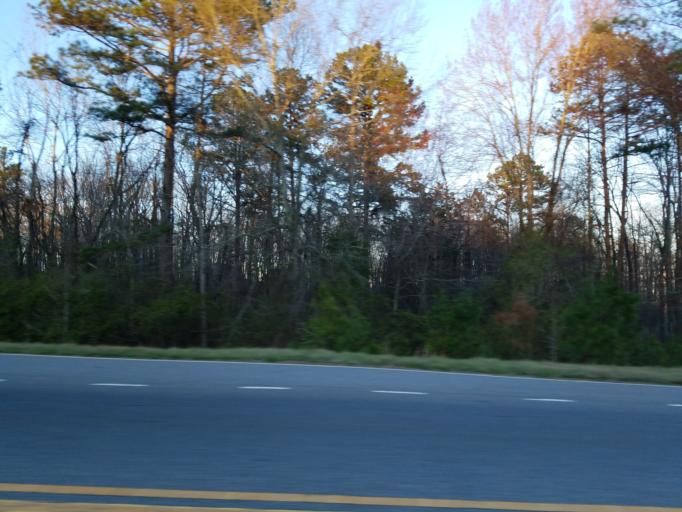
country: US
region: Georgia
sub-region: Hall County
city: Oakwood
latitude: 34.3192
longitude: -84.0028
